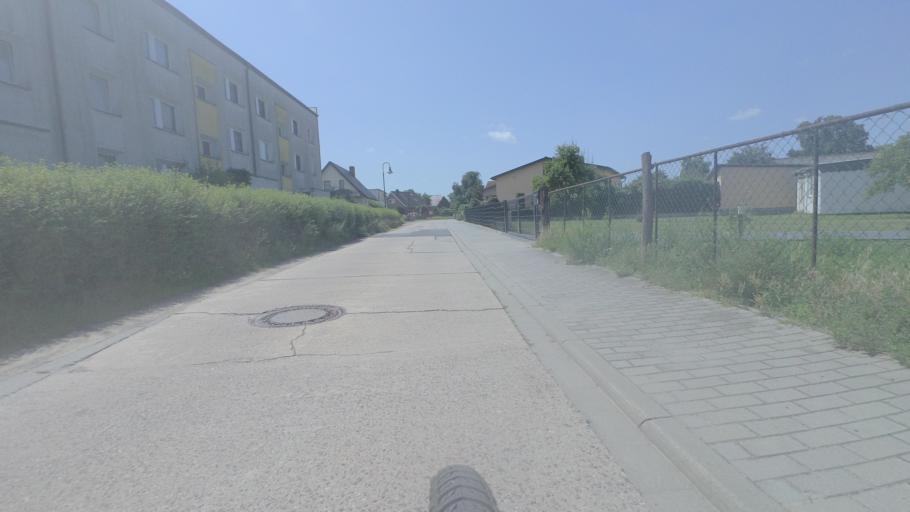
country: DE
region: Brandenburg
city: Rangsdorf
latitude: 52.2558
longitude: 13.3802
